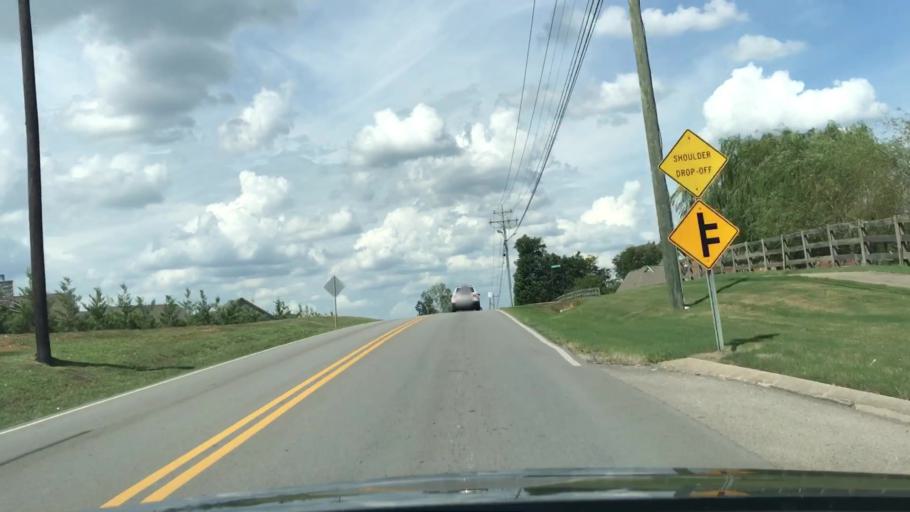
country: US
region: Tennessee
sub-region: Maury County
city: Spring Hill
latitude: 35.7544
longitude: -86.8835
